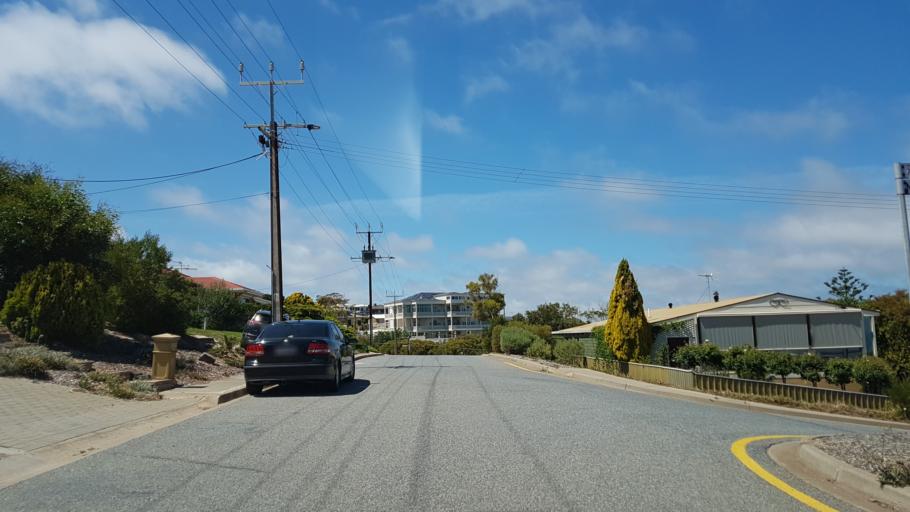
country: AU
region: South Australia
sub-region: Marion
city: Marino
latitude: -35.0638
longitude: 138.5074
